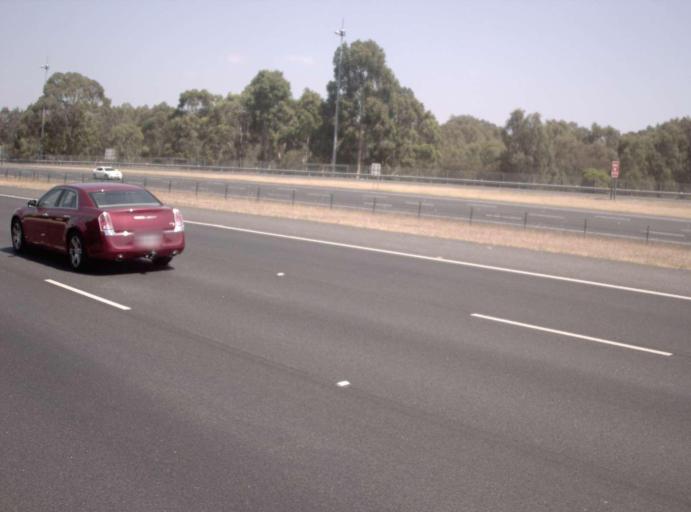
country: AU
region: Victoria
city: Ivanhoe East
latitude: -37.7854
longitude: 145.0609
